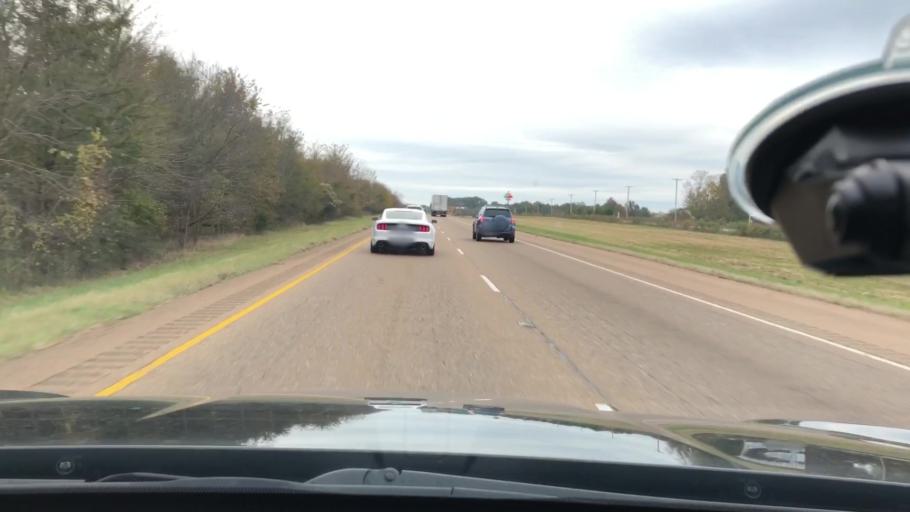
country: US
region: Arkansas
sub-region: Nevada County
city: Prescott
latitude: 33.8226
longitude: -93.4068
